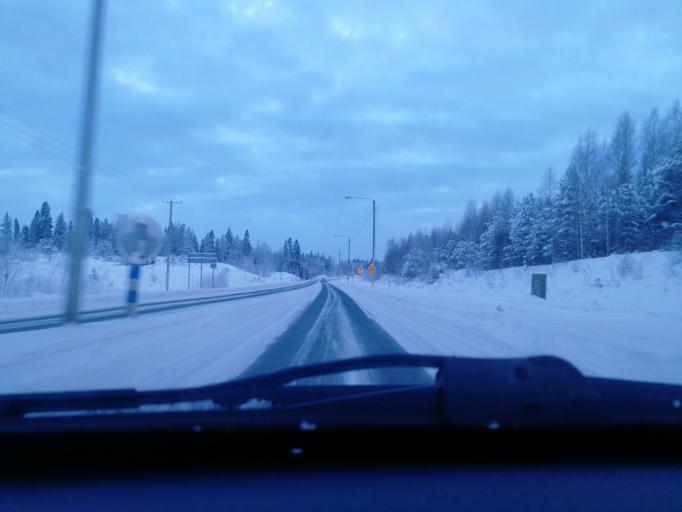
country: FI
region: Pirkanmaa
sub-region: Tampere
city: Tampere
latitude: 61.4411
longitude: 23.8748
